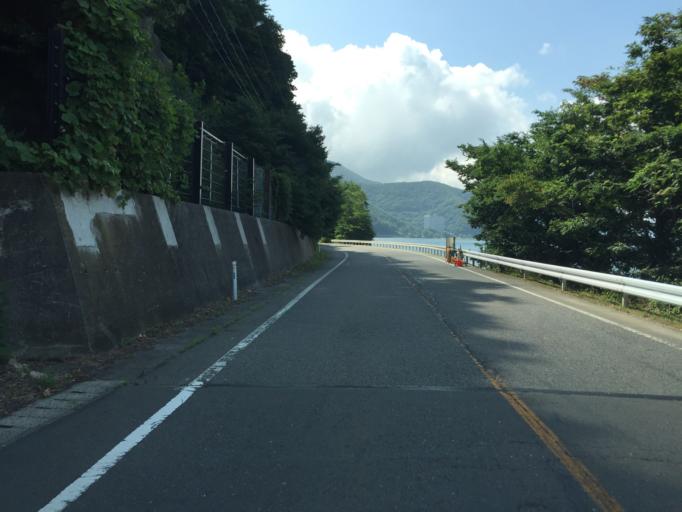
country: JP
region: Fukushima
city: Inawashiro
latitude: 37.4731
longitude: 140.1508
